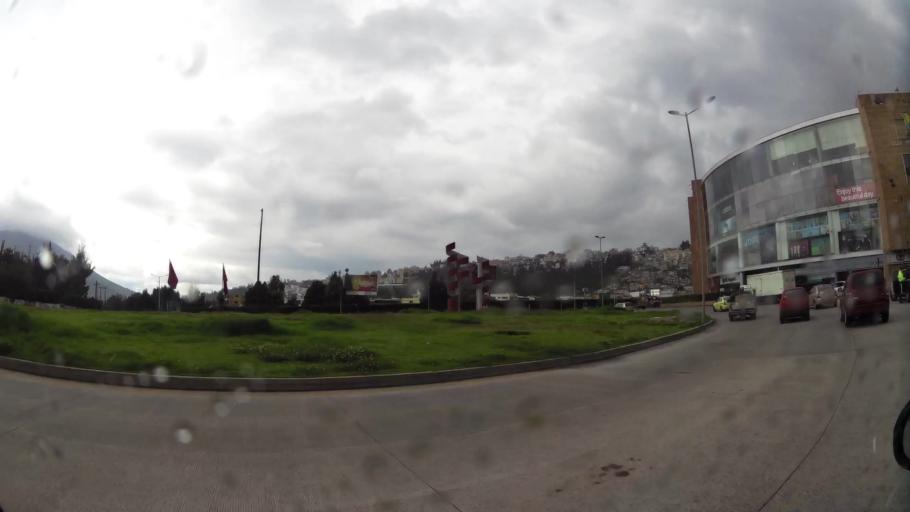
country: EC
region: Pichincha
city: Quito
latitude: -0.1023
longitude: -78.4911
